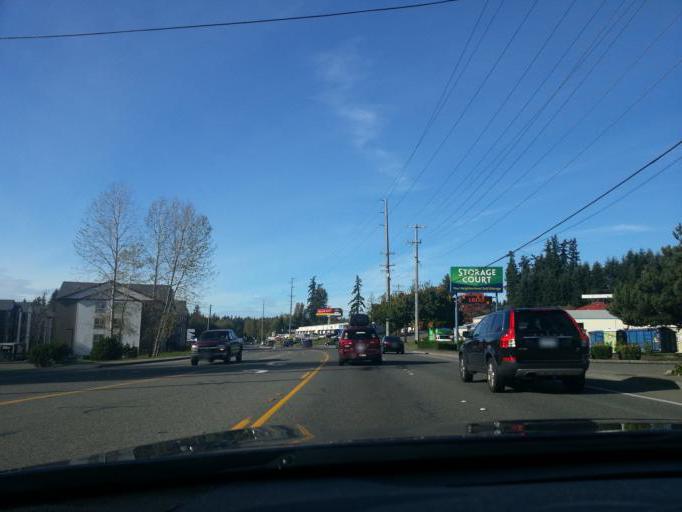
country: US
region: Washington
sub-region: Snohomish County
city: Mill Creek
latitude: 47.8358
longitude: -122.2115
